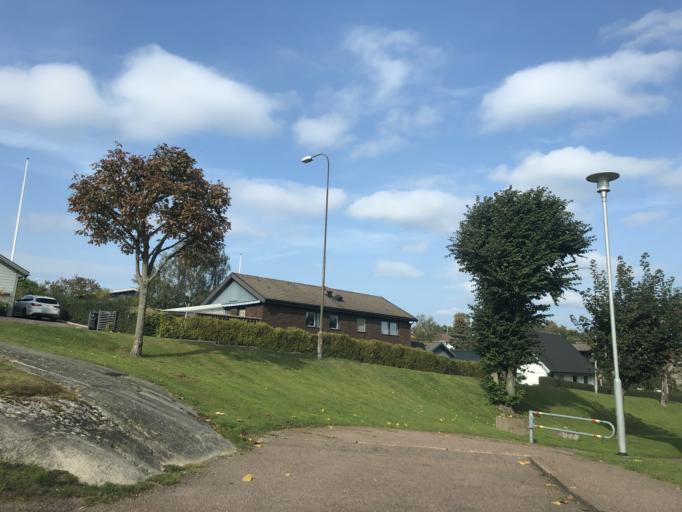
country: SE
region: Vaestra Goetaland
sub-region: Goteborg
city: Majorna
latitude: 57.6508
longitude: 11.8899
